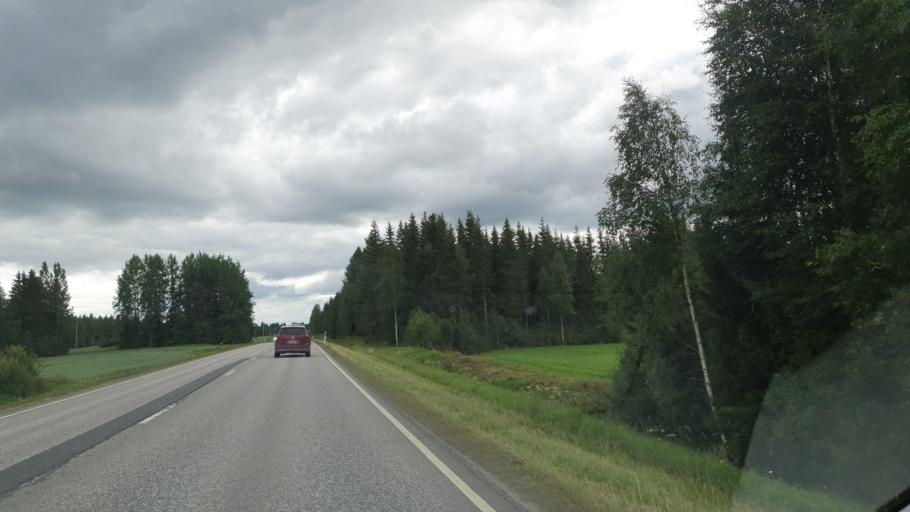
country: FI
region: Northern Savo
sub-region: Ylae-Savo
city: Sonkajaervi
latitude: 63.7346
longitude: 27.3777
